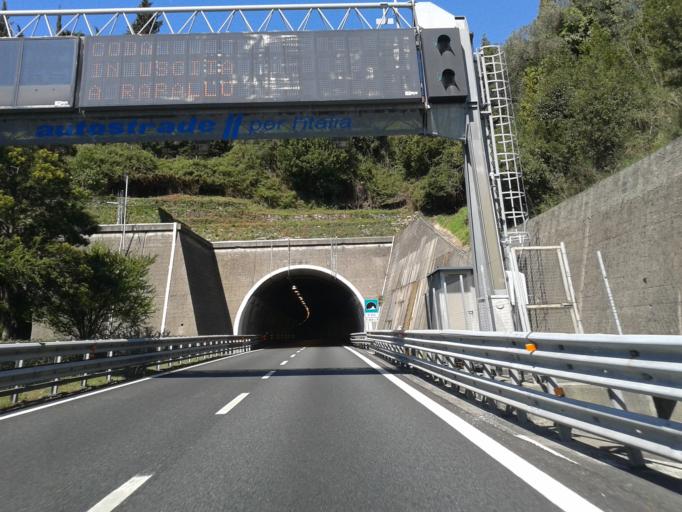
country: IT
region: Liguria
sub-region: Provincia di Genova
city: Chiavari
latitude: 44.3238
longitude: 9.3343
